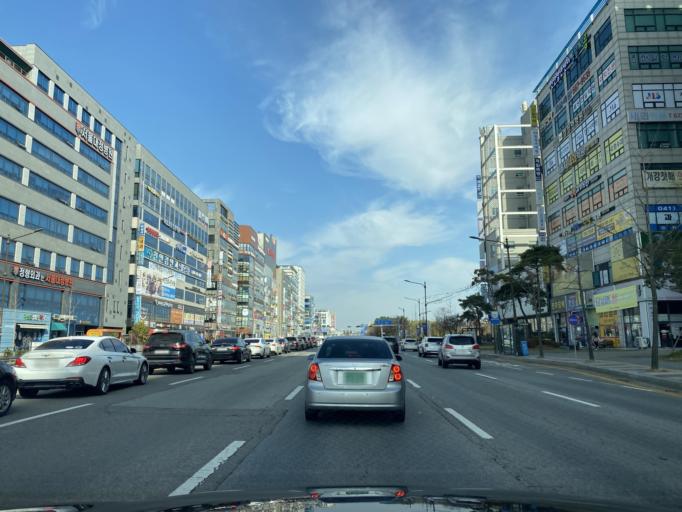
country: KR
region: Chungcheongnam-do
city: Cheonan
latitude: 36.8109
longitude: 127.1083
